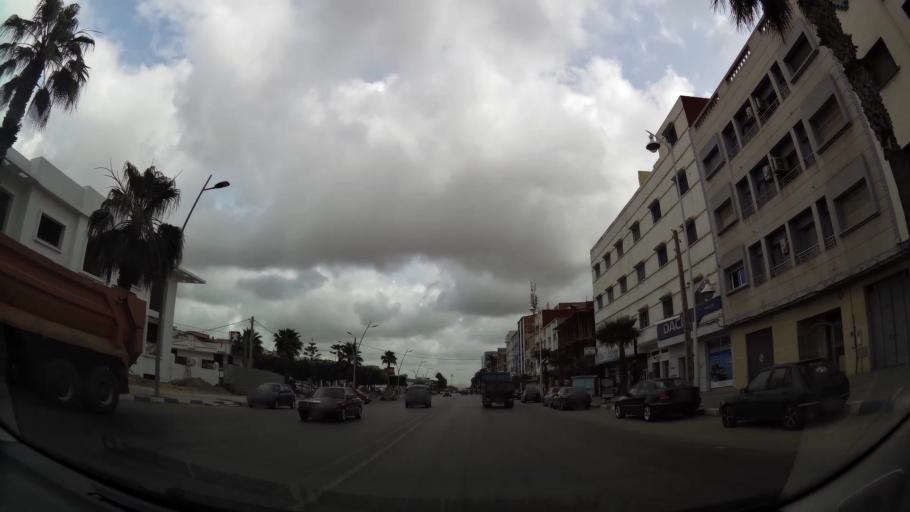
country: MA
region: Oriental
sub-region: Nador
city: Nador
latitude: 35.1558
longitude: -2.9296
